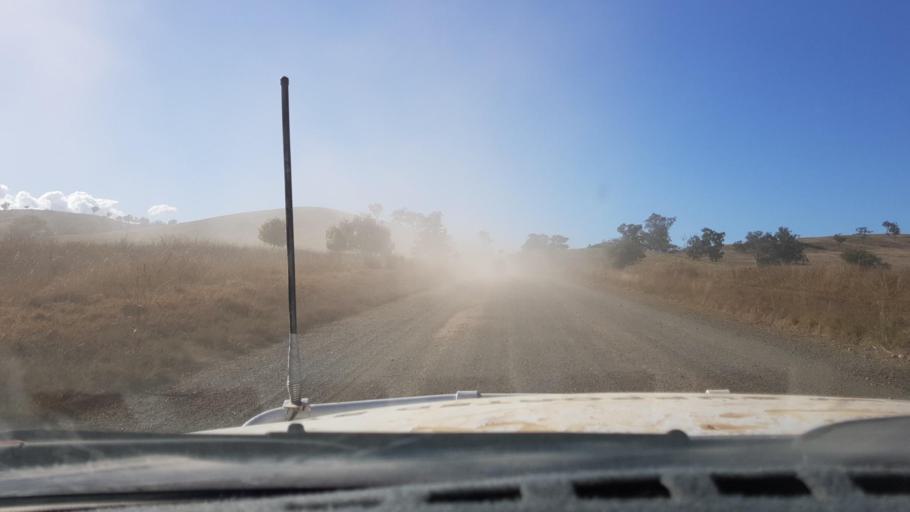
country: AU
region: New South Wales
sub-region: Narrabri
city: Blair Athol
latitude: -30.6731
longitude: 150.3948
